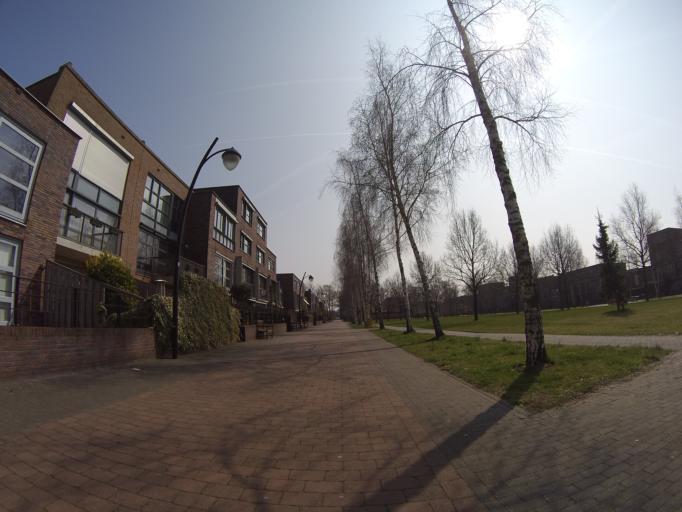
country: NL
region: Utrecht
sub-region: Gemeente Amersfoort
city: Hoogland
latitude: 52.2002
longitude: 5.4144
